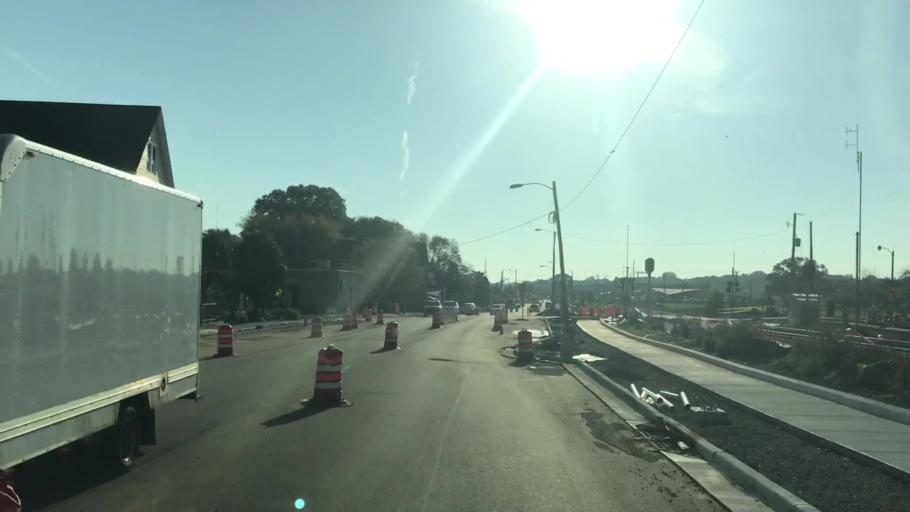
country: US
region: Wisconsin
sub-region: Milwaukee County
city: Wauwatosa
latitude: 43.0482
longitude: -88.0031
